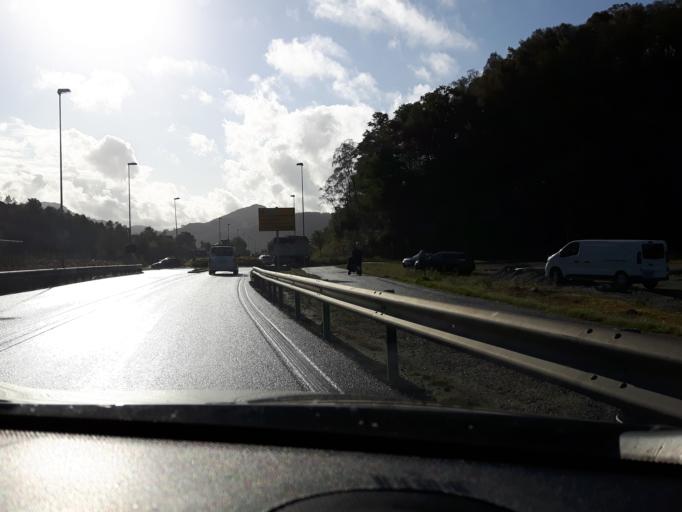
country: NO
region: Rogaland
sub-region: Gjesdal
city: Algard
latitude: 58.7695
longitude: 5.8557
